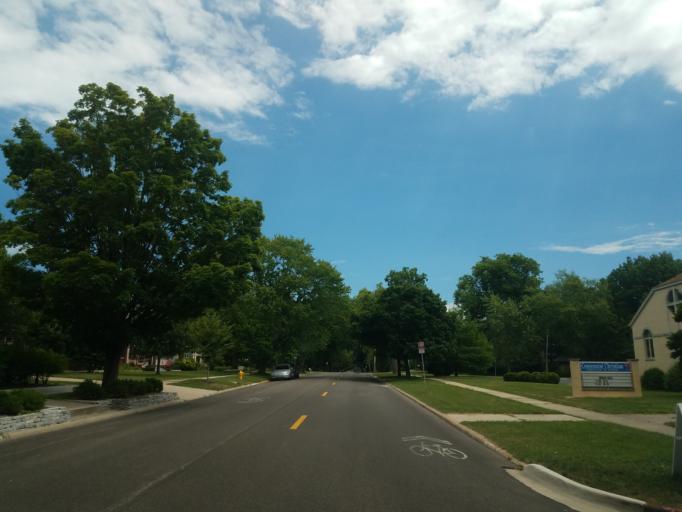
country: US
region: Illinois
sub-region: McLean County
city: Bloomington
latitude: 40.4782
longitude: -88.9731
